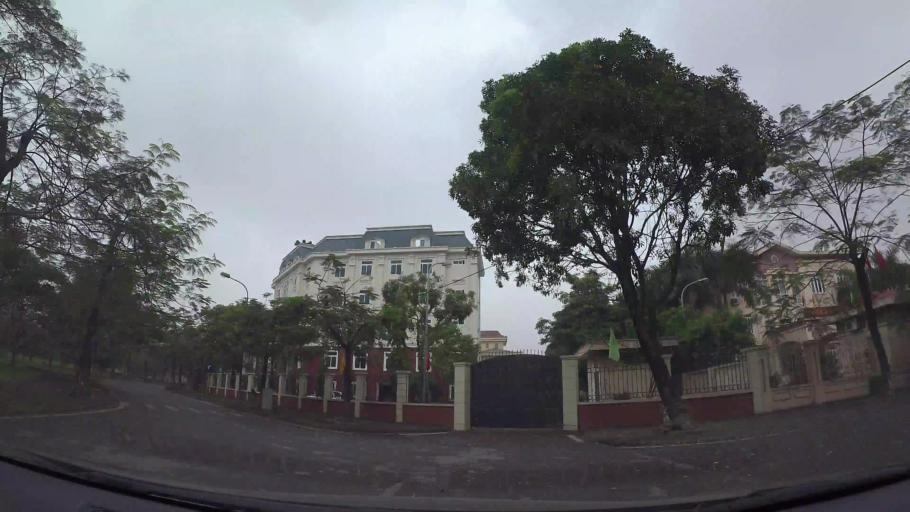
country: VN
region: Ha Noi
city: Van Dien
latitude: 20.9675
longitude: 105.8473
